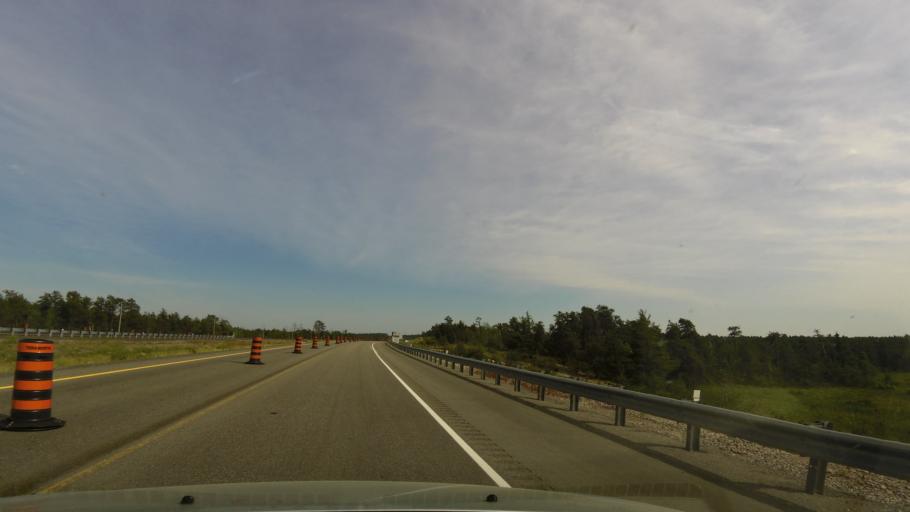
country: CA
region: Ontario
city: Greater Sudbury
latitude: 46.0683
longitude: -80.6363
